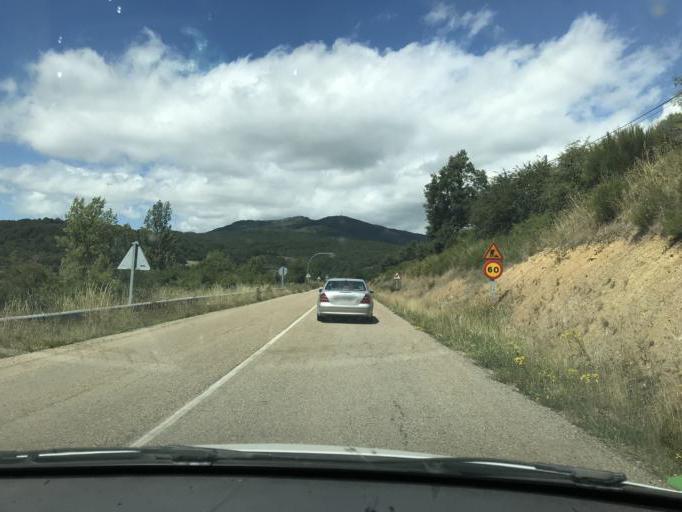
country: ES
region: Castille and Leon
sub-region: Provincia de Palencia
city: Polentinos
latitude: 42.9217
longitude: -4.4867
